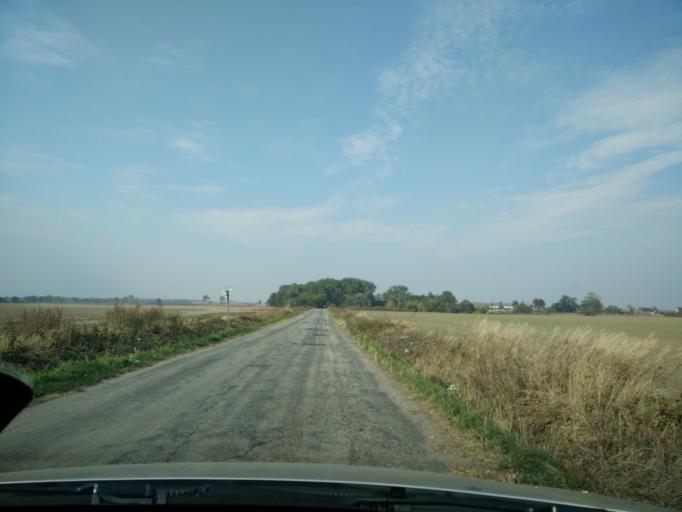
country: PL
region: Greater Poland Voivodeship
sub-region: Powiat sredzki
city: Dominowo
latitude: 52.2835
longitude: 17.3231
